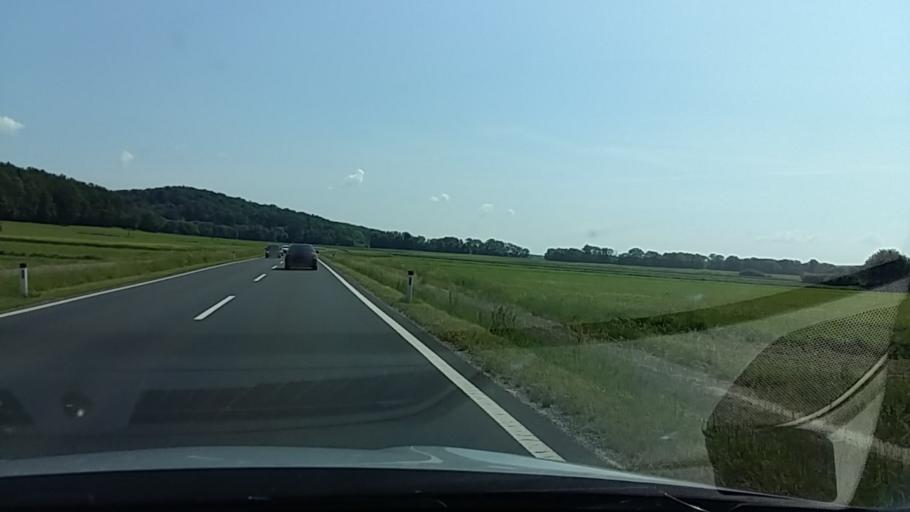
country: AT
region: Burgenland
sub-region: Politischer Bezirk Jennersdorf
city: Weichselbaum
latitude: 46.9443
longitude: 16.1977
